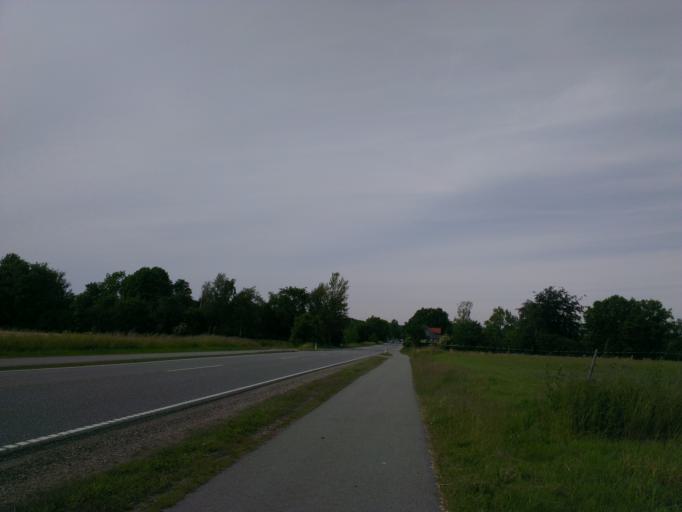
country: DK
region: Capital Region
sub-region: Frederikssund Kommune
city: Skibby
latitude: 55.7703
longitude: 11.9596
